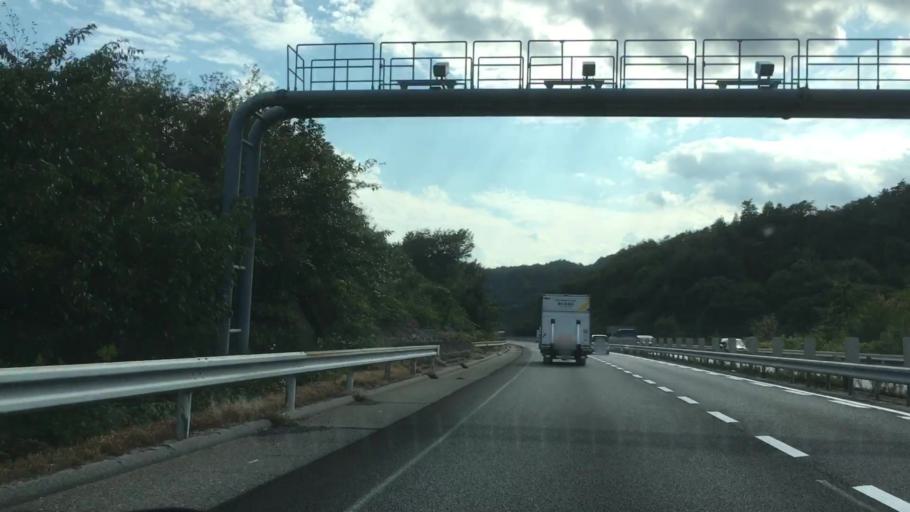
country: JP
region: Hiroshima
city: Ono-hara
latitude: 34.3188
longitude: 132.2834
